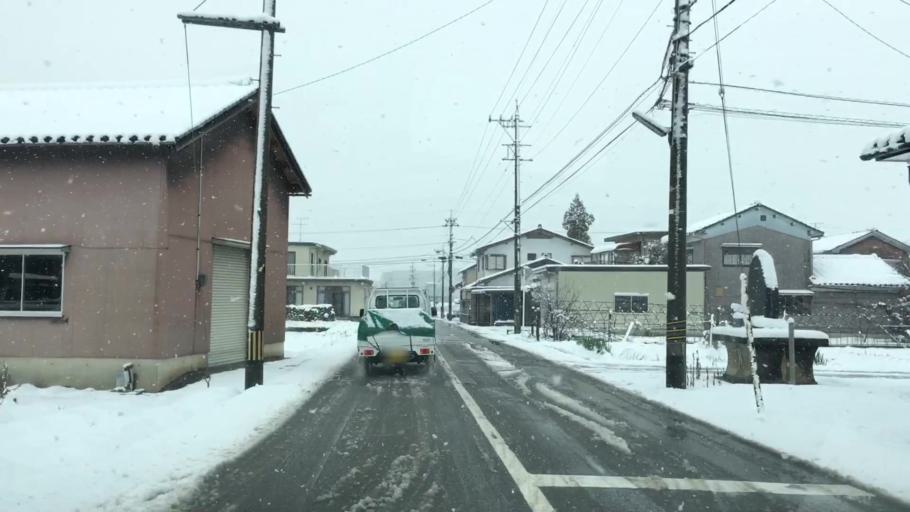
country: JP
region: Toyama
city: Kamiichi
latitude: 36.6932
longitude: 137.3373
